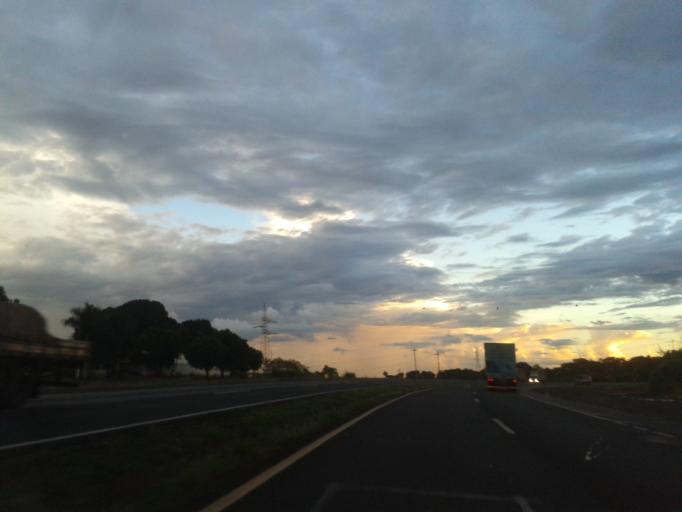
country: BR
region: Minas Gerais
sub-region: Monte Alegre De Minas
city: Monte Alegre de Minas
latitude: -18.7711
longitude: -49.0732
